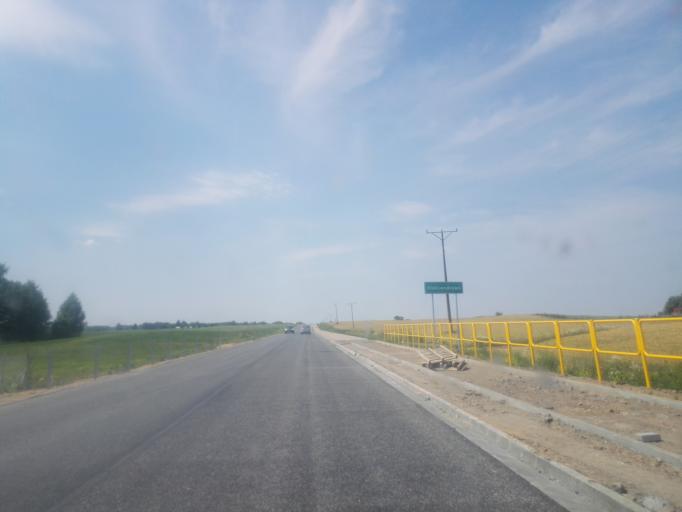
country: PL
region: Podlasie
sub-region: Powiat sejnenski
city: Krasnopol
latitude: 54.0962
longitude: 23.1727
